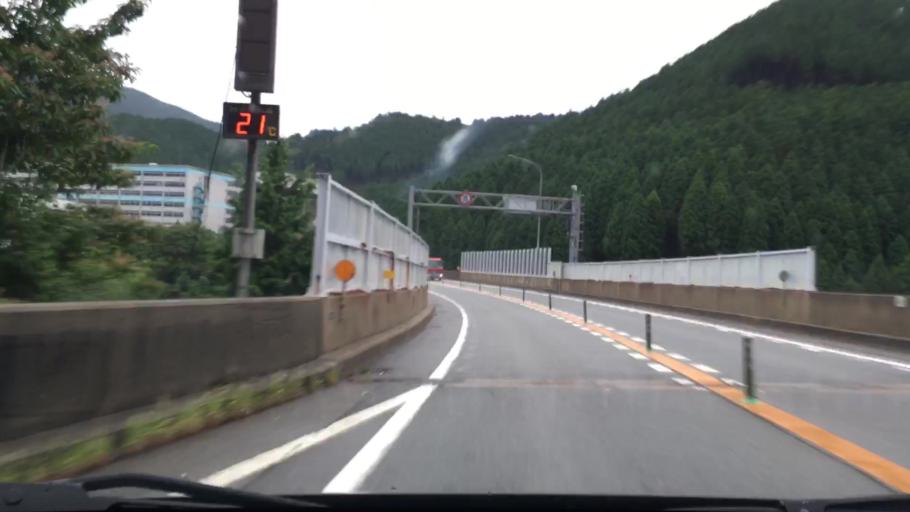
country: JP
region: Hyogo
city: Nishiwaki
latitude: 35.1508
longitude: 134.7865
